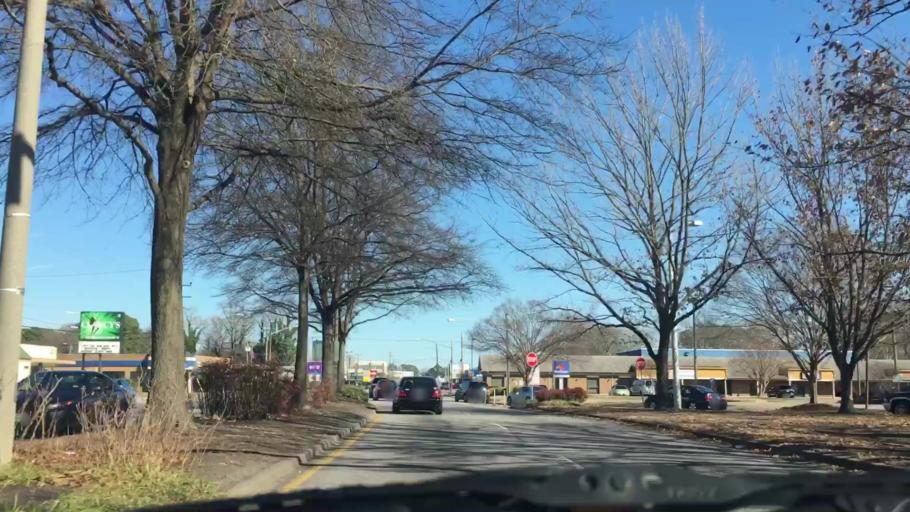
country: US
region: Virginia
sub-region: City of Norfolk
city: Norfolk
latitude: 36.9152
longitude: -76.2384
